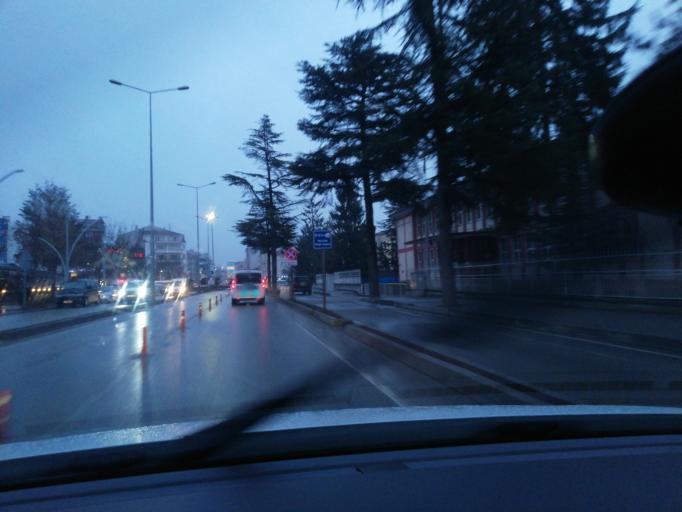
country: TR
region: Bolu
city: Bolu
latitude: 40.7306
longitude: 31.5986
